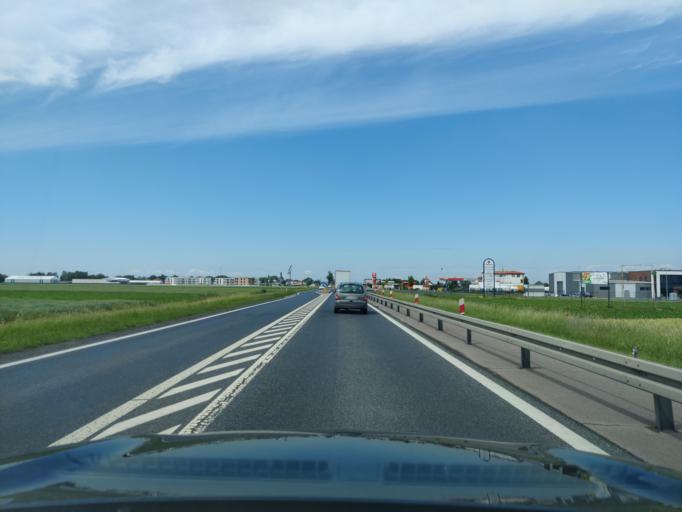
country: PL
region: Greater Poland Voivodeship
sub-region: Powiat grodziski
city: Granowo
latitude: 52.2220
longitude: 16.5478
